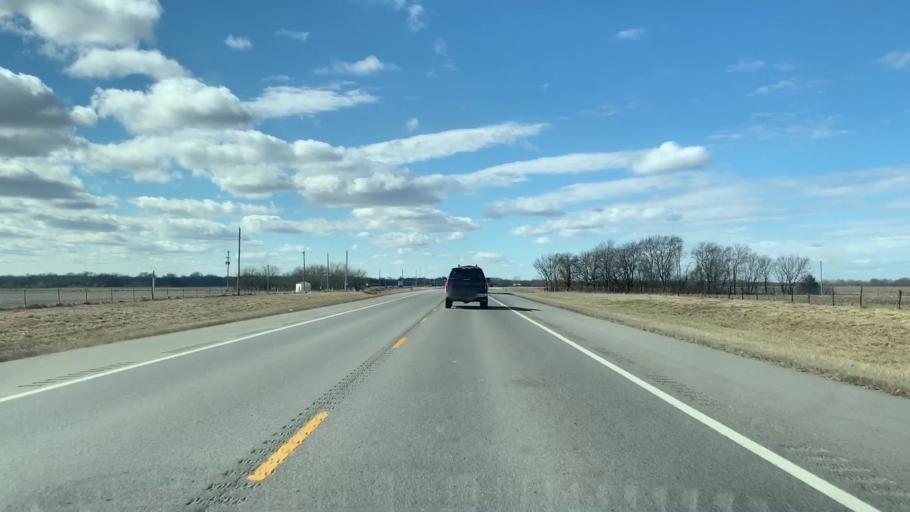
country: US
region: Kansas
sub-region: Cherokee County
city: Columbus
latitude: 37.3398
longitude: -94.8665
